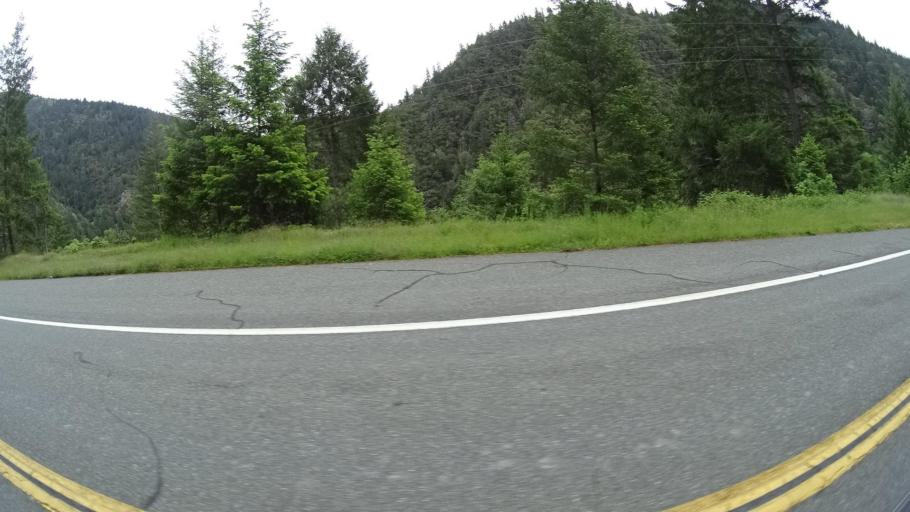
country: US
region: California
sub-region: Humboldt County
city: Willow Creek
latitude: 41.2707
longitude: -123.6061
